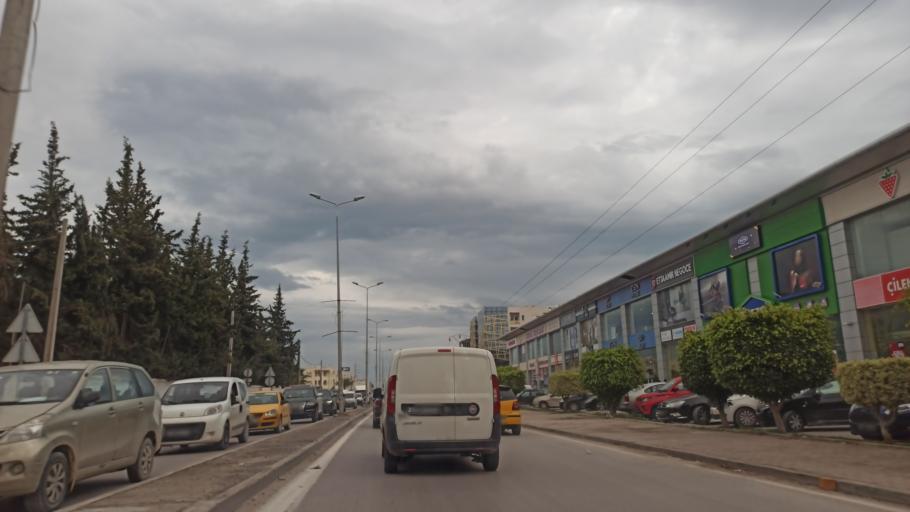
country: TN
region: Ariana
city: Ariana
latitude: 36.8676
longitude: 10.2243
